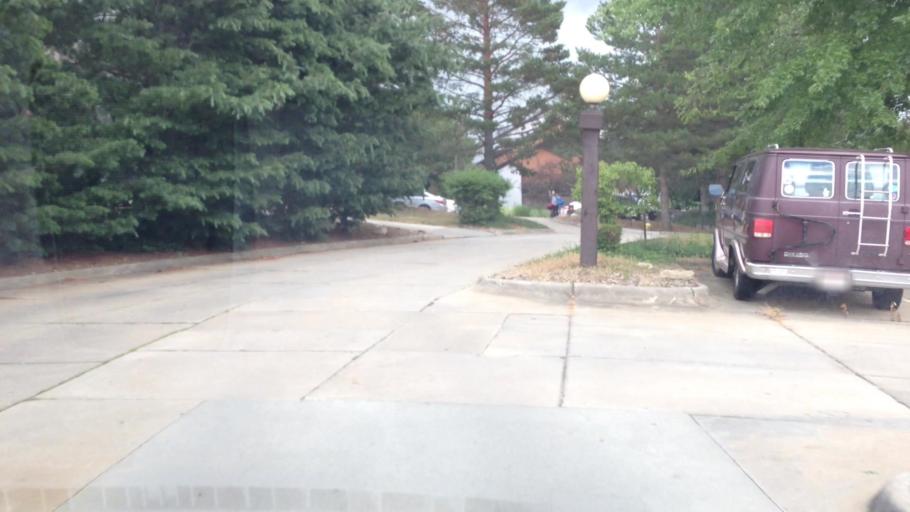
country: US
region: Ohio
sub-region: Summit County
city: Barberton
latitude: 41.0440
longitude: -81.5811
